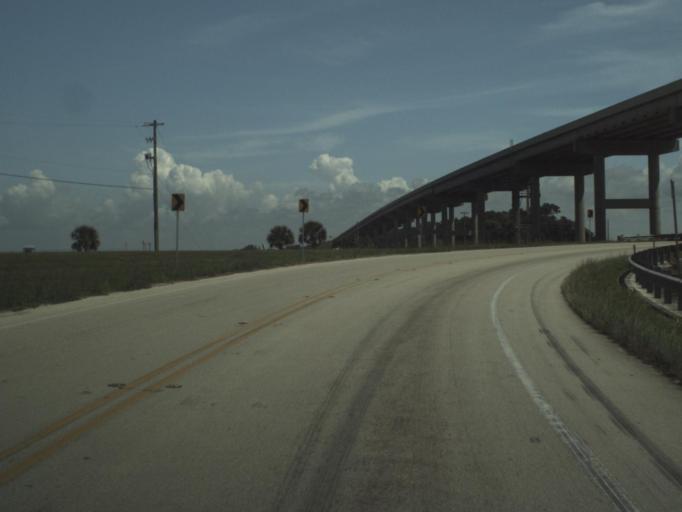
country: US
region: Florida
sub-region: Martin County
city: Indiantown
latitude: 26.9837
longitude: -80.6170
